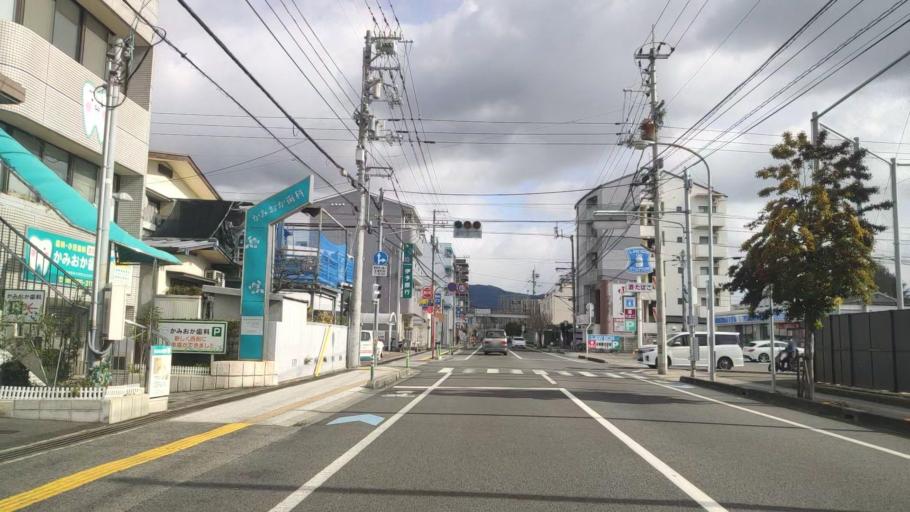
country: JP
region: Ehime
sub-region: Shikoku-chuo Shi
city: Matsuyama
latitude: 33.8525
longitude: 132.7651
